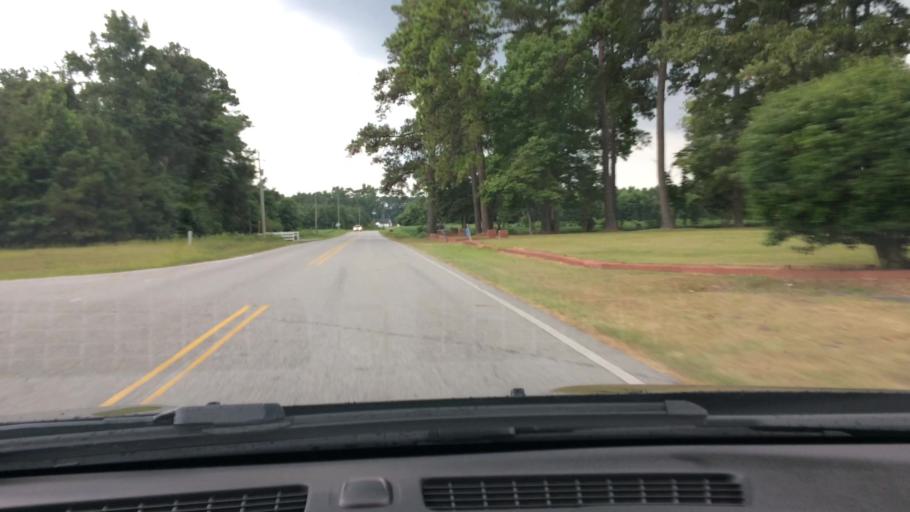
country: US
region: North Carolina
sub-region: Pitt County
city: Ayden
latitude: 35.4817
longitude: -77.3771
